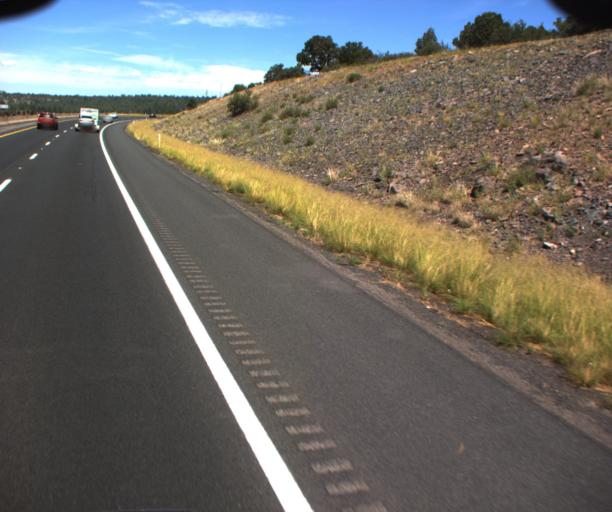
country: US
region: Arizona
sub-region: Yavapai County
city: Village of Oak Creek (Big Park)
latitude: 34.8114
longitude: -111.6080
